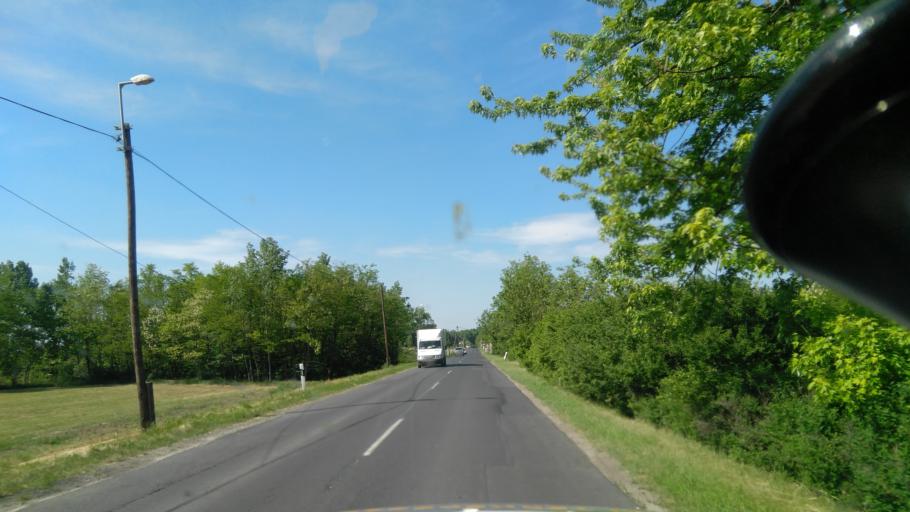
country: HU
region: Bekes
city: Gyula
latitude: 46.6709
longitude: 21.3002
